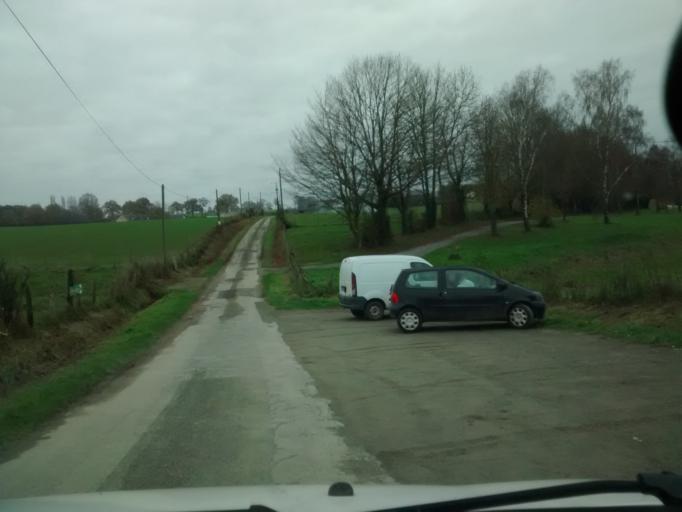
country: FR
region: Brittany
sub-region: Departement d'Ille-et-Vilaine
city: Erbree
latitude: 48.0961
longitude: -1.1571
